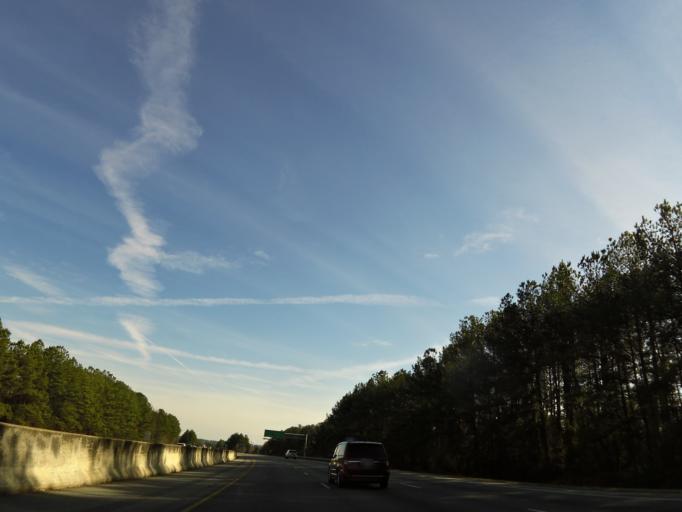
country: US
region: Alabama
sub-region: Russell County
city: Phenix City
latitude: 32.5247
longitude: -84.9582
